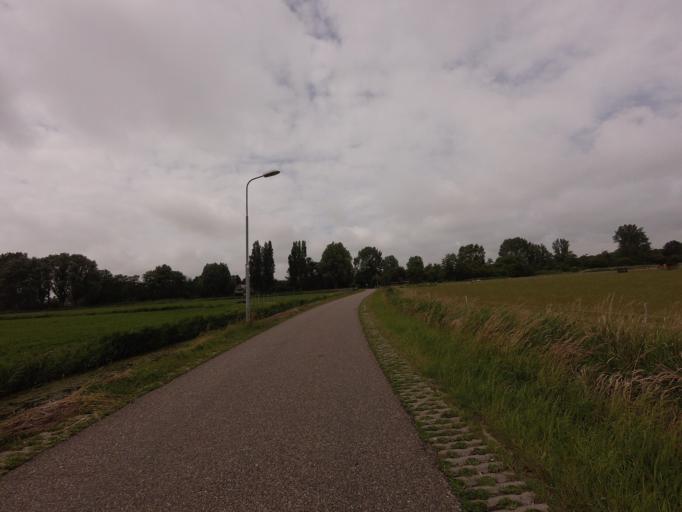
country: NL
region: North Holland
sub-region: Gemeente Schagen
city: Schagen
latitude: 52.7788
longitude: 4.7889
